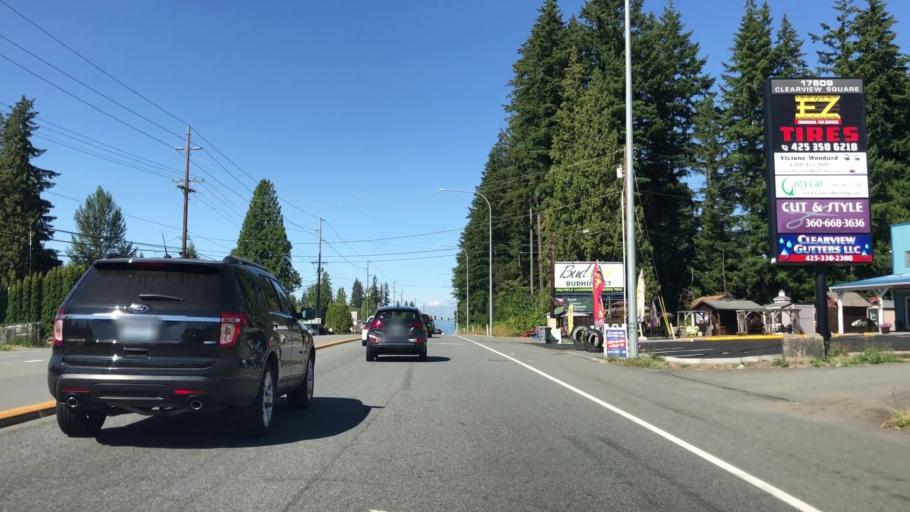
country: US
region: Washington
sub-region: Snohomish County
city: Clearview
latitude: 47.8350
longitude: -122.1253
